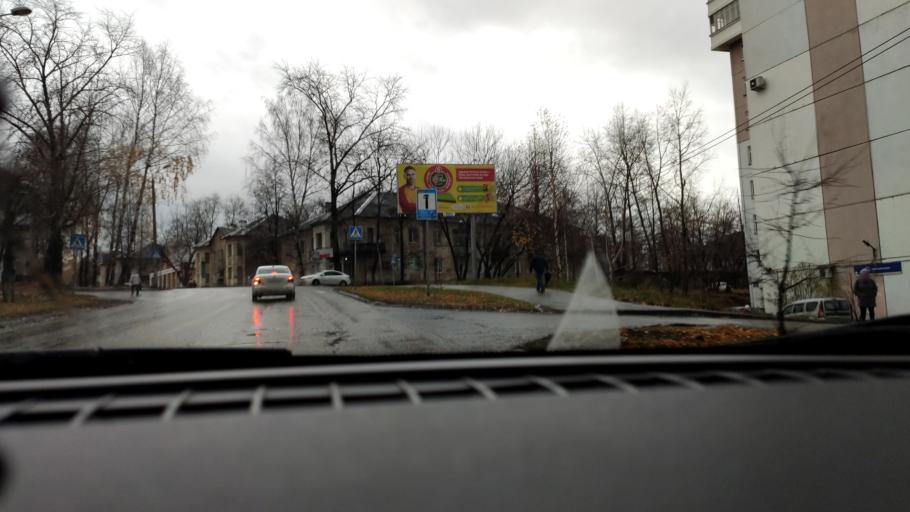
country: RU
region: Perm
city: Perm
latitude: 58.1124
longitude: 56.3681
